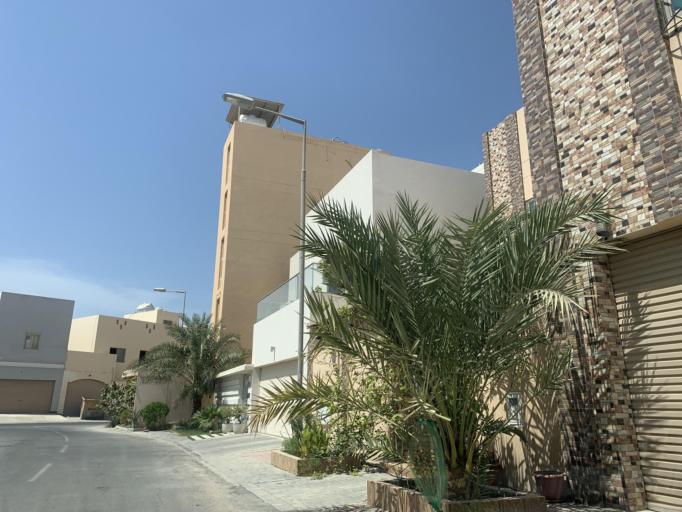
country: BH
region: Northern
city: Madinat `Isa
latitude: 26.1809
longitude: 50.4758
